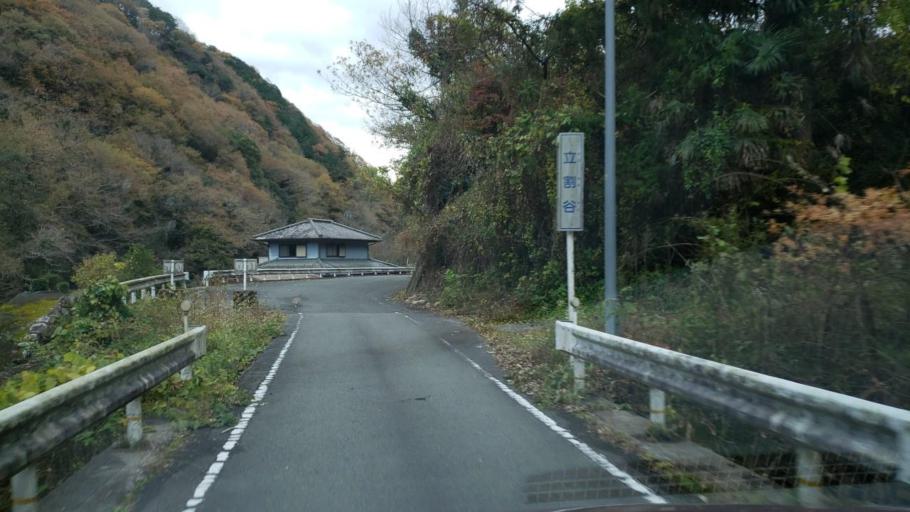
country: JP
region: Tokushima
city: Wakimachi
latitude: 34.1259
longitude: 134.2270
